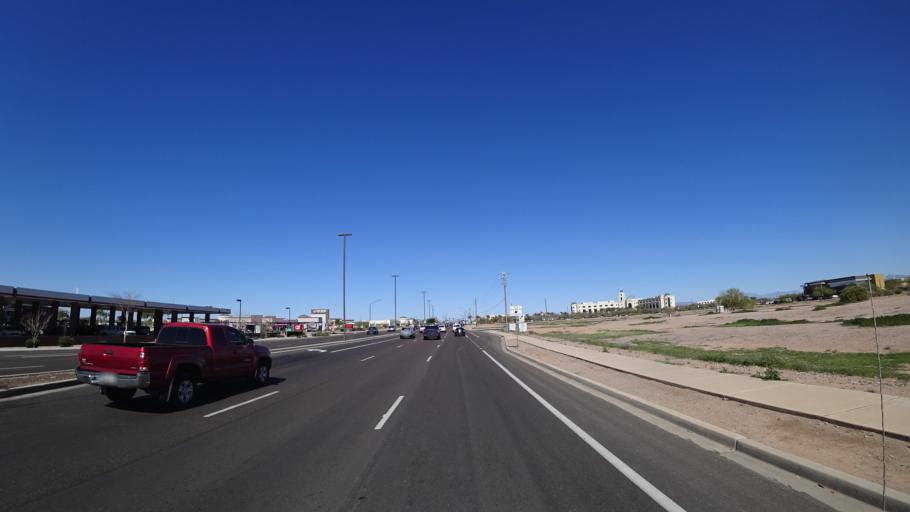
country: US
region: Arizona
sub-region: Maricopa County
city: Gilbert
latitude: 33.2822
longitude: -111.7552
